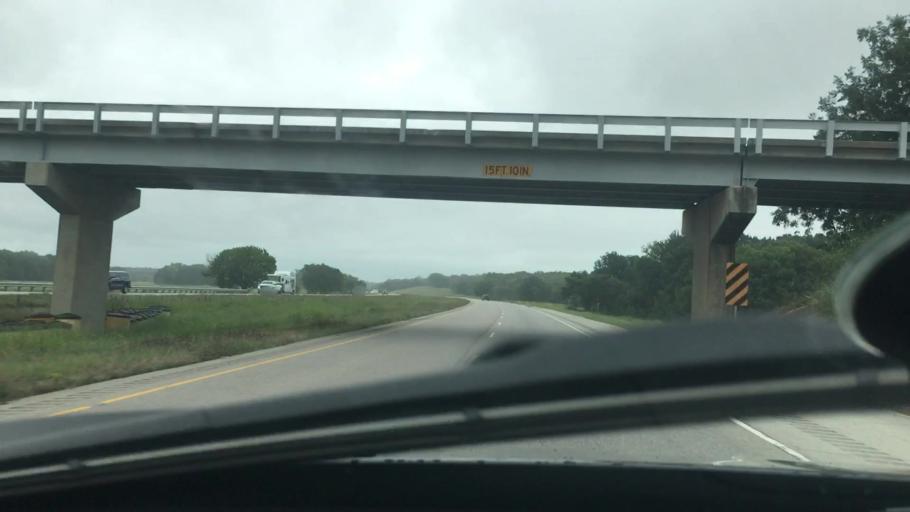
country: US
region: Oklahoma
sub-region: Okfuskee County
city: Boley
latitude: 35.3860
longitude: -96.4239
